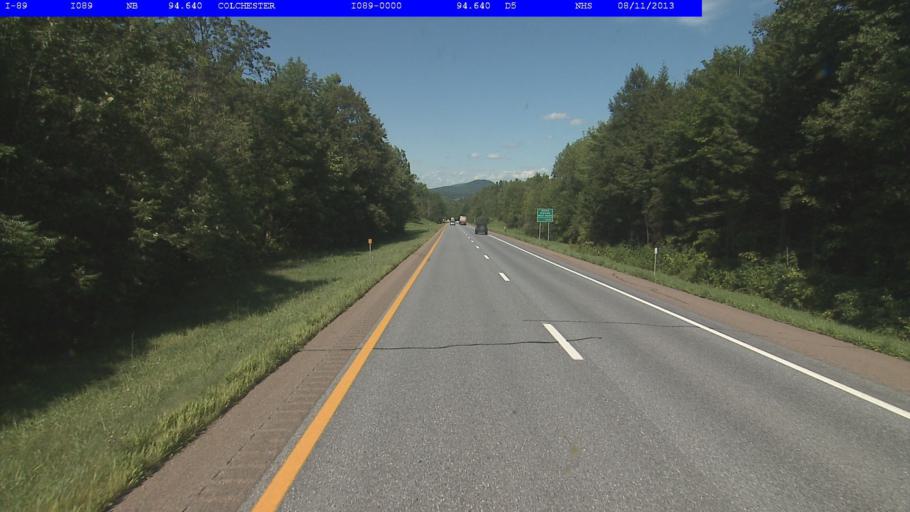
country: US
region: Vermont
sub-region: Chittenden County
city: Colchester
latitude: 44.5461
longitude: -73.1913
